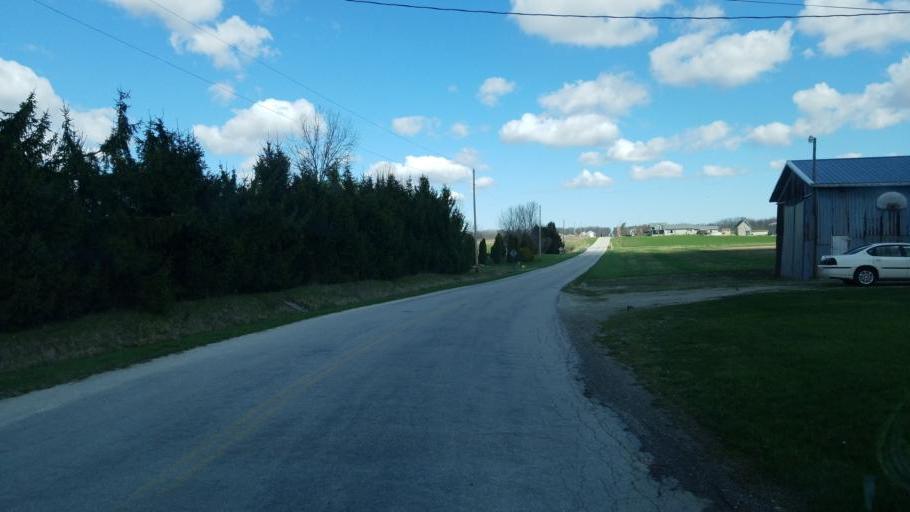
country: US
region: Ohio
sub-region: Sandusky County
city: Mount Carmel
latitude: 41.1686
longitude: -82.9382
